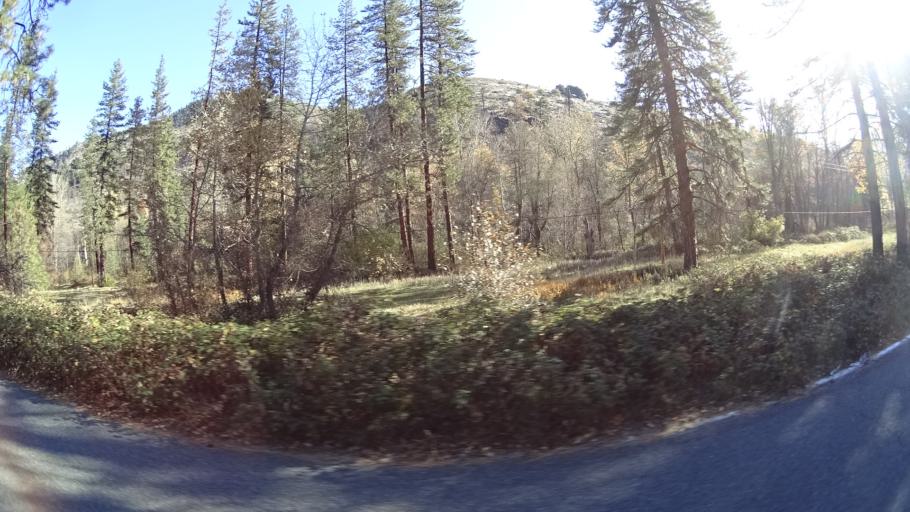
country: US
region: California
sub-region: Siskiyou County
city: Yreka
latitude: 41.8745
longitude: -122.8202
